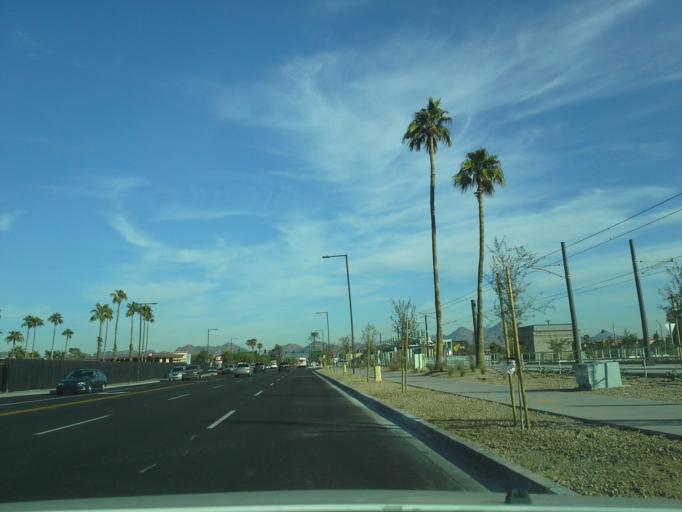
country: US
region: Arizona
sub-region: Maricopa County
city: Glendale
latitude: 33.5676
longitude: -112.1025
